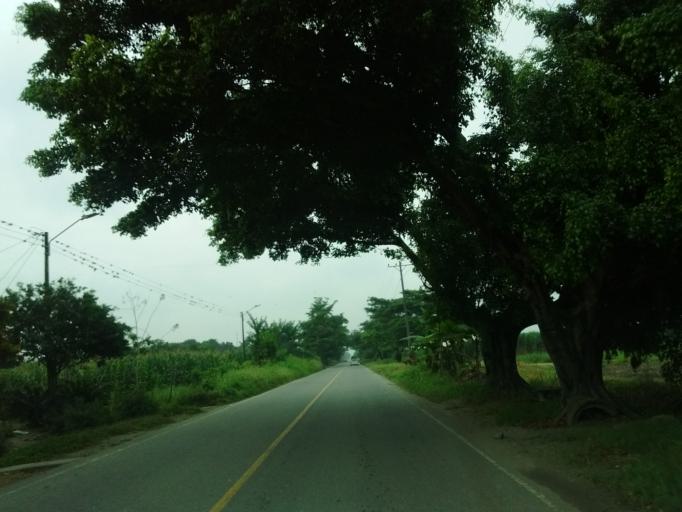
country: CO
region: Cauca
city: Padilla
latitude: 3.2247
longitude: -76.3596
